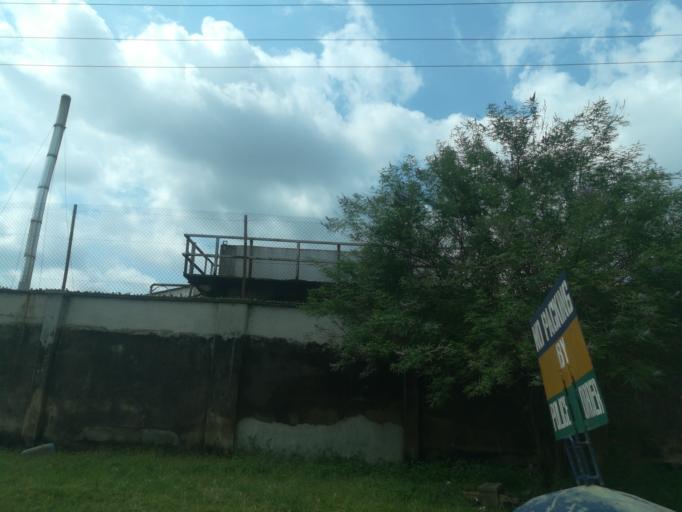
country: NG
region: Oyo
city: Ibadan
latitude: 7.3583
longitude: 3.8497
